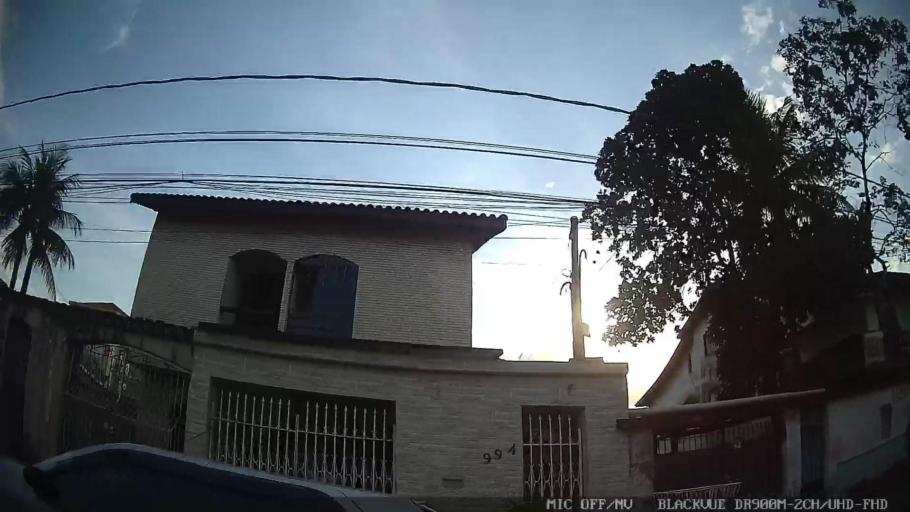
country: BR
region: Sao Paulo
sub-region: Cubatao
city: Cubatao
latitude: -23.8985
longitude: -46.4256
